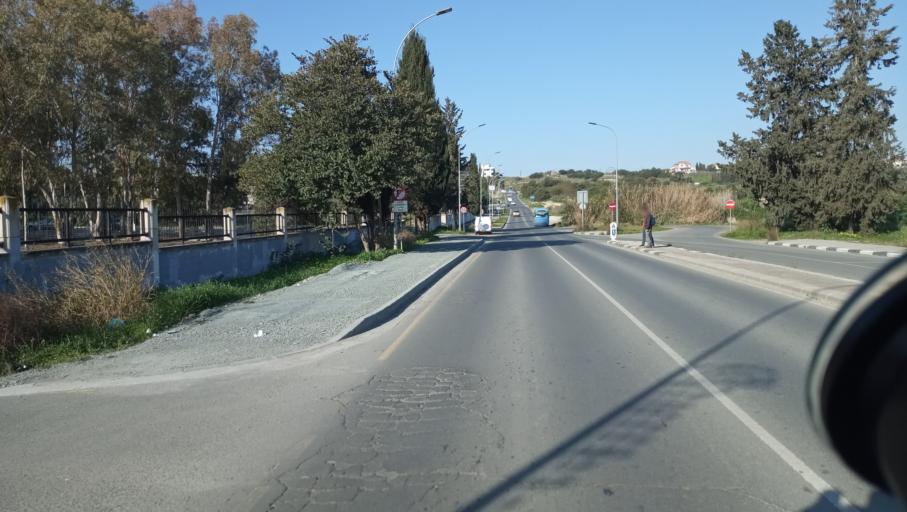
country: CY
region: Lefkosia
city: Nicosia
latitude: 35.1483
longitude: 33.3136
